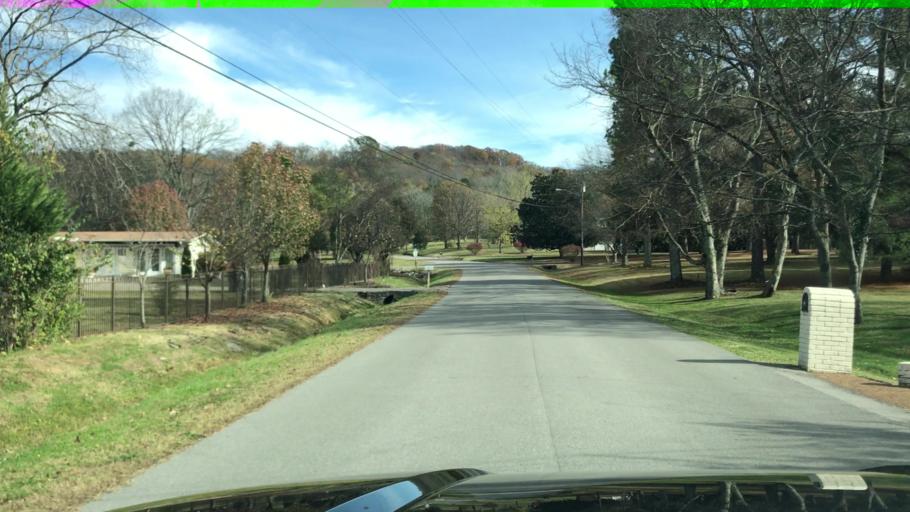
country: US
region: Tennessee
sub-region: Davidson County
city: Forest Hills
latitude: 36.0250
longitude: -86.8485
